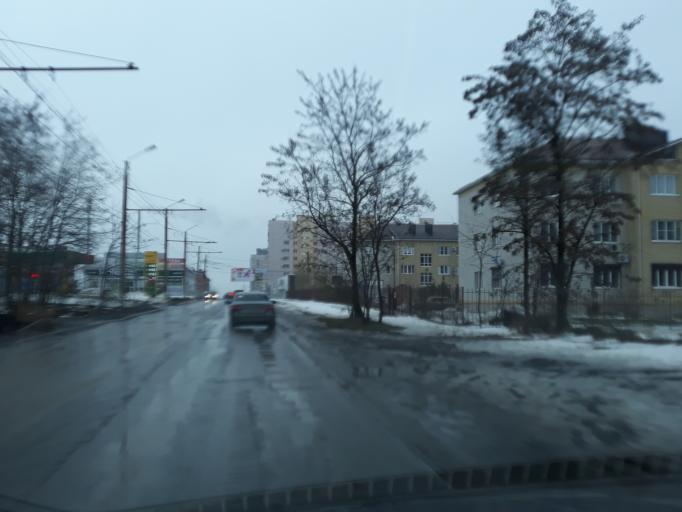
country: RU
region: Rostov
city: Taganrog
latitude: 47.2786
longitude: 38.9220
